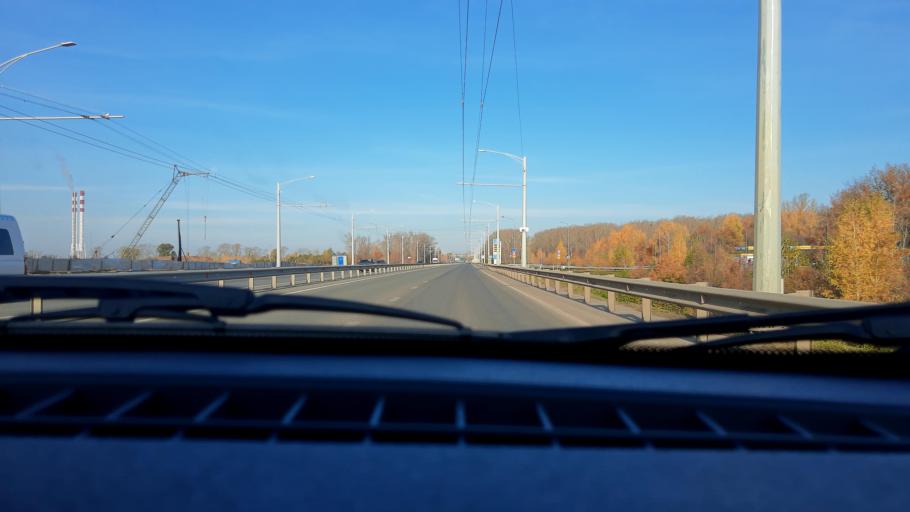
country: RU
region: Bashkortostan
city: Mikhaylovka
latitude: 54.7711
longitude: 55.9050
